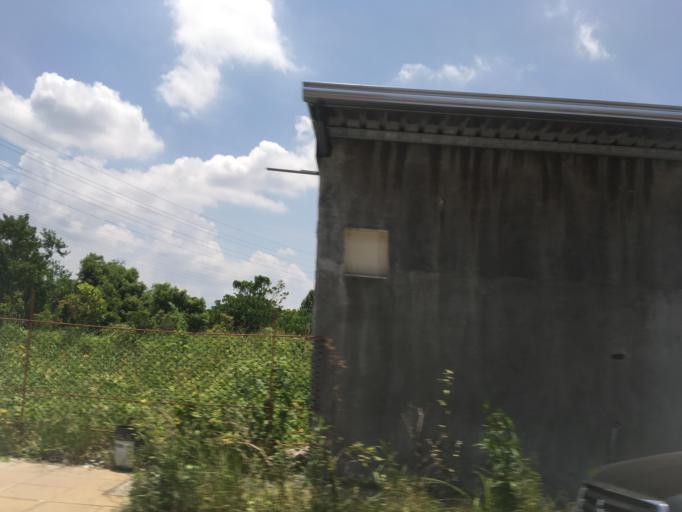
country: TW
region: Taiwan
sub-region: Yilan
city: Yilan
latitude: 24.6585
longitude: 121.7609
